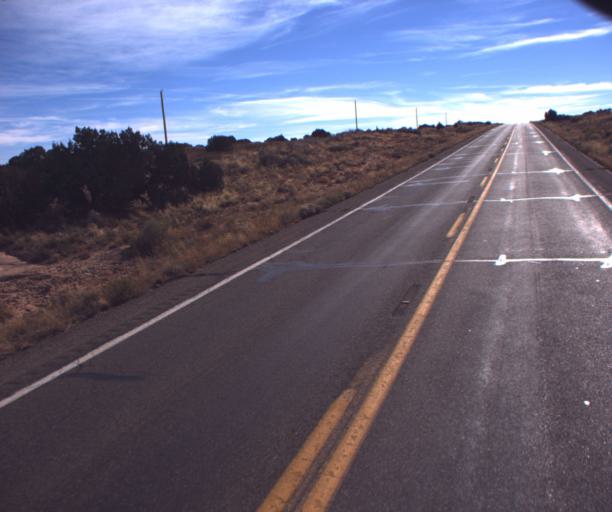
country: US
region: Arizona
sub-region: Coconino County
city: Kaibito
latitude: 36.6001
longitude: -111.1702
